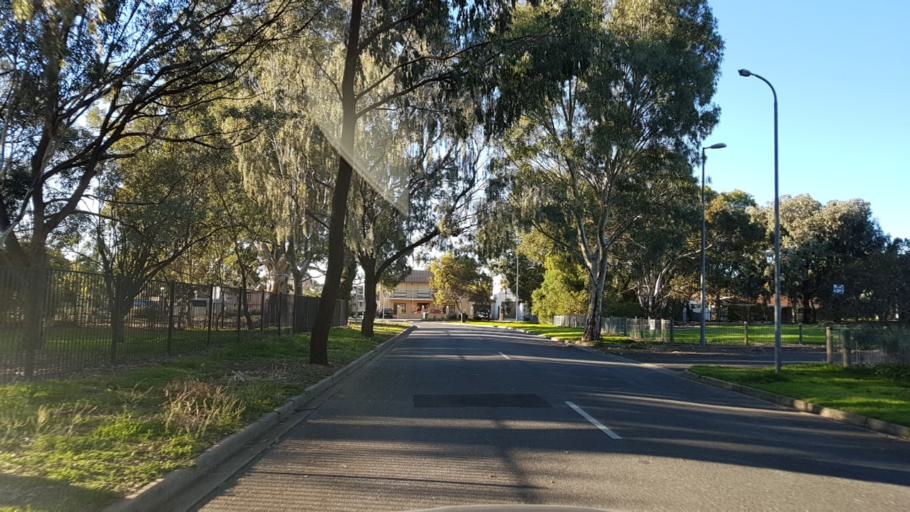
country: AU
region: South Australia
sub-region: Campbelltown
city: Campbelltown
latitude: -34.8772
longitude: 138.6529
